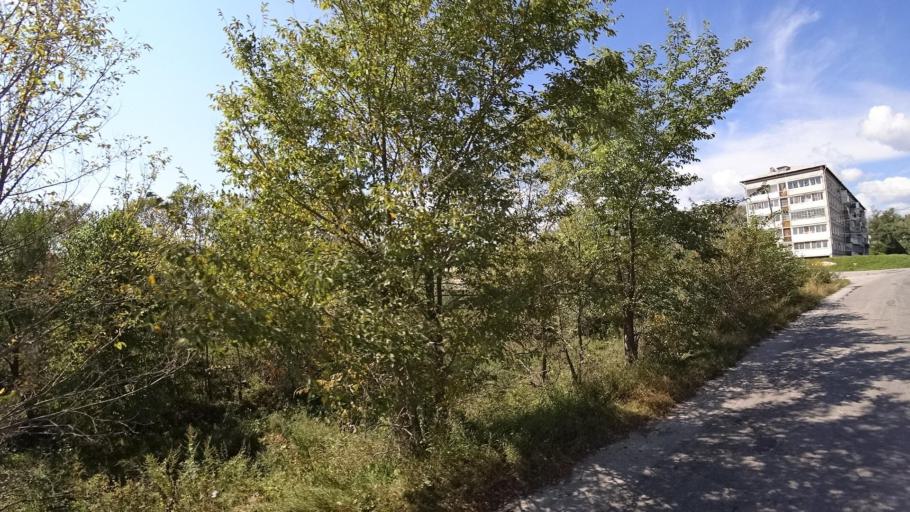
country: RU
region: Jewish Autonomous Oblast
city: Londoko
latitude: 49.0090
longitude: 131.8877
